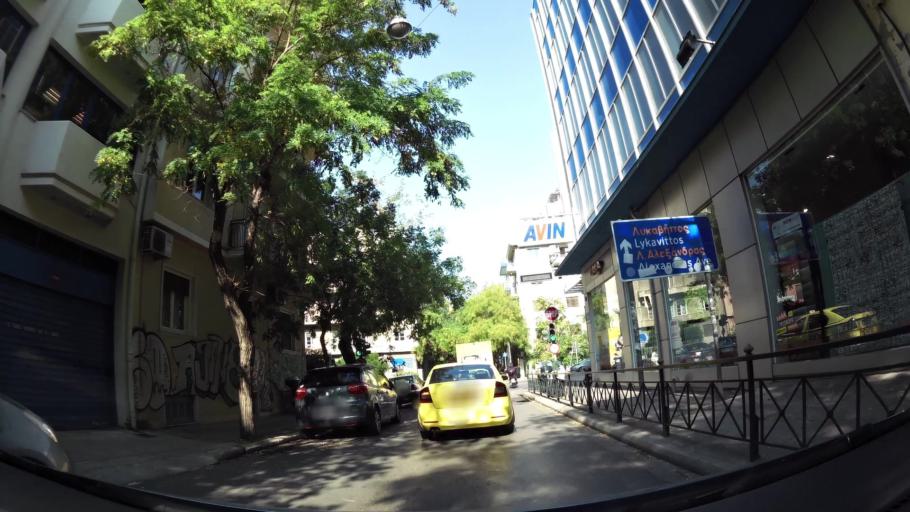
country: GR
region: Attica
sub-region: Nomarchia Athinas
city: Kaisariani
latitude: 37.9810
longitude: 23.7587
